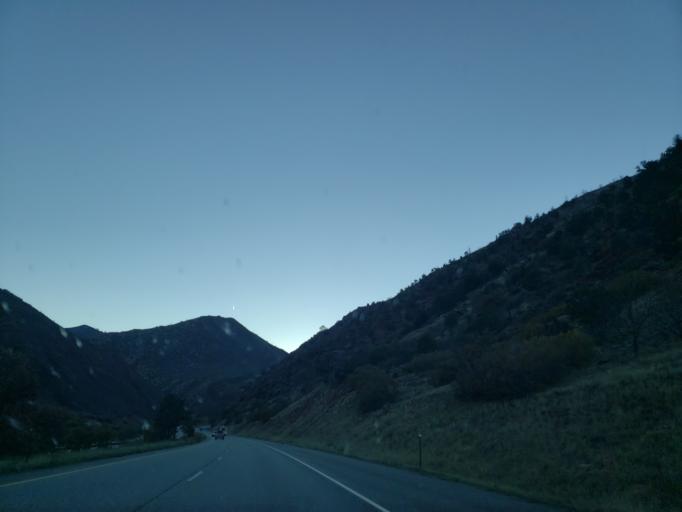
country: US
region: Colorado
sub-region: Garfield County
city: Glenwood Springs
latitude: 39.5604
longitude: -107.3889
